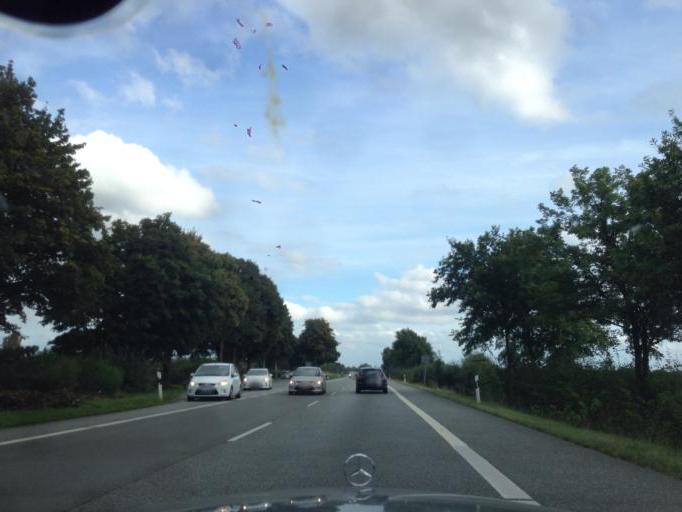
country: DE
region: Schleswig-Holstein
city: Negernbotel
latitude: 53.9730
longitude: 10.2277
